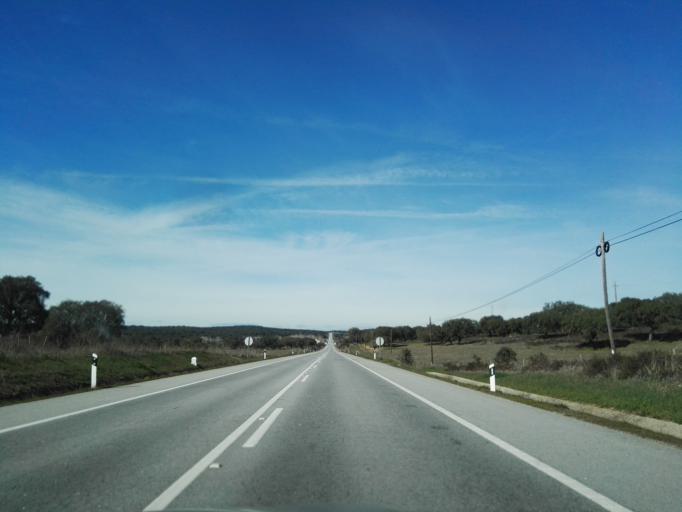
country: PT
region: Portalegre
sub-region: Arronches
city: Arronches
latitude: 39.1523
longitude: -7.3124
